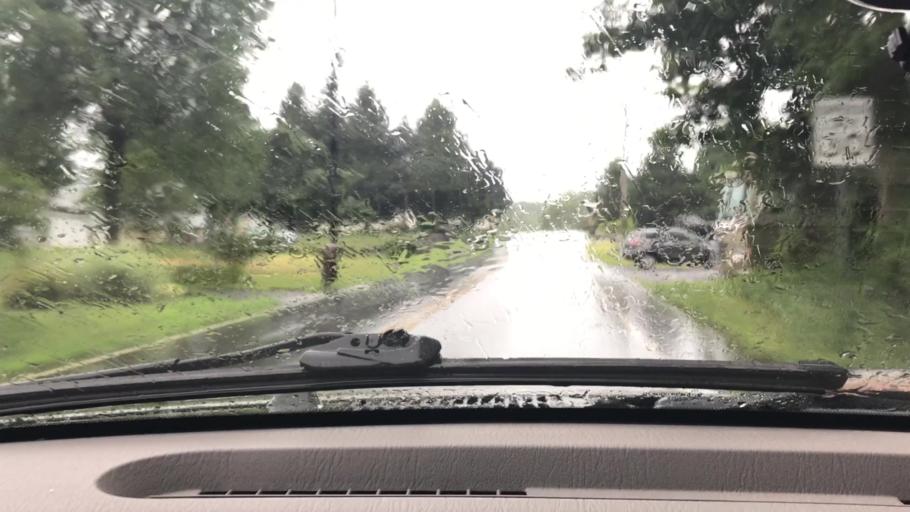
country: US
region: Pennsylvania
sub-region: Lancaster County
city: Elizabethtown
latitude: 40.1484
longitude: -76.6298
